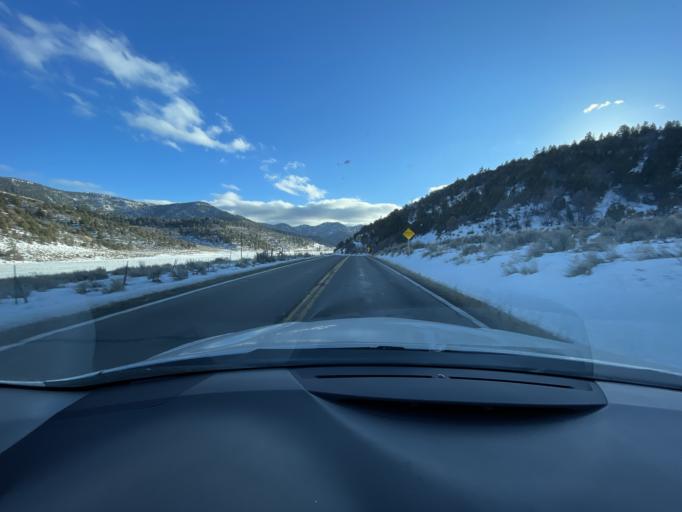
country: US
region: Colorado
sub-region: Rio Blanco County
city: Rangely
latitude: 39.6483
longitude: -108.7890
